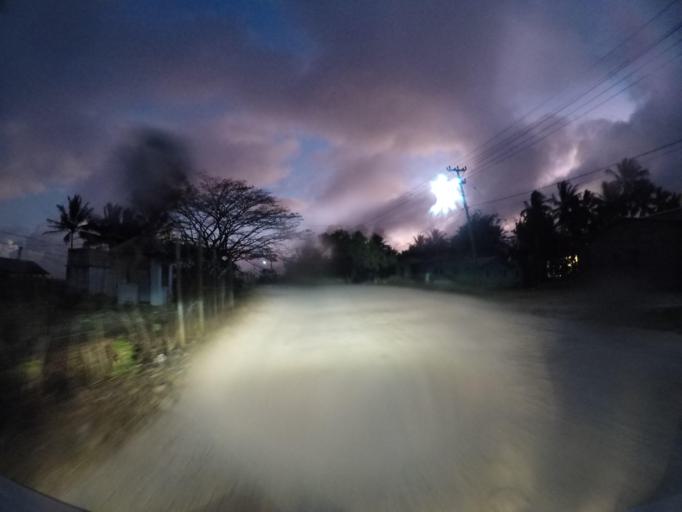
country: TL
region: Lautem
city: Lospalos
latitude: -8.4456
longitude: 127.0036
